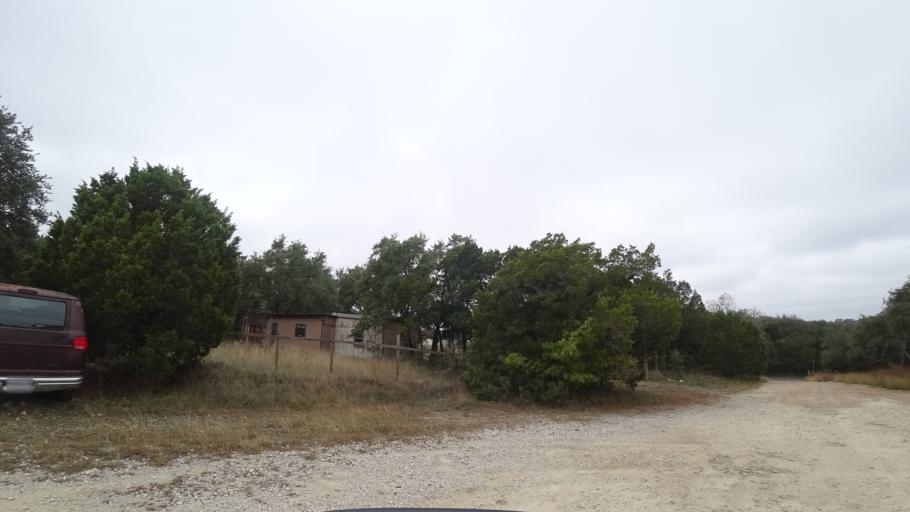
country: US
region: Texas
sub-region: Travis County
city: Barton Creek
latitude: 30.2367
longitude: -97.9068
